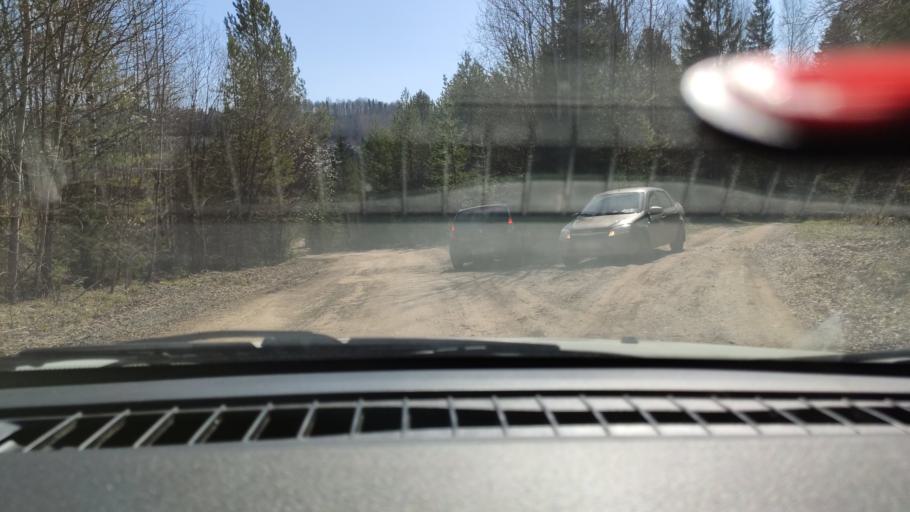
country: RU
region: Perm
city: Bershet'
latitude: 57.7228
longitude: 56.4032
